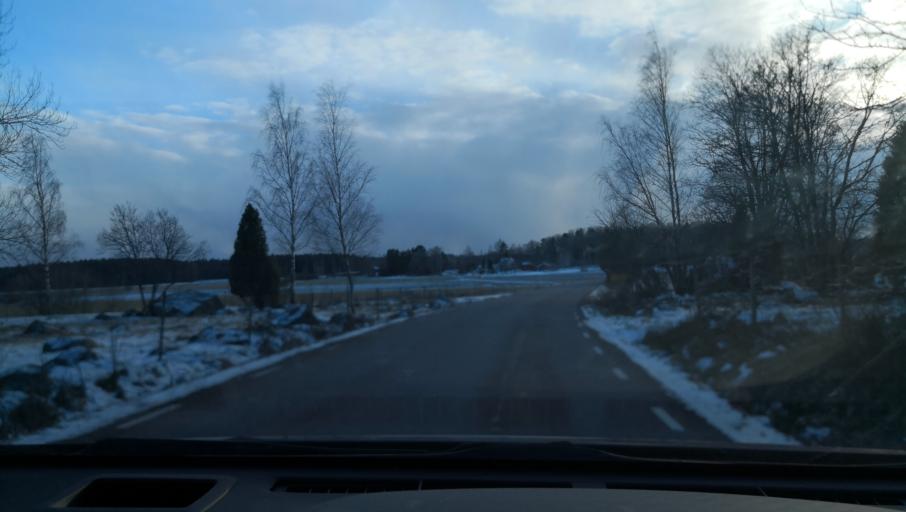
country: SE
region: Vaestmanland
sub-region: Vasteras
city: Tillberga
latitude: 59.6461
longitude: 16.7464
